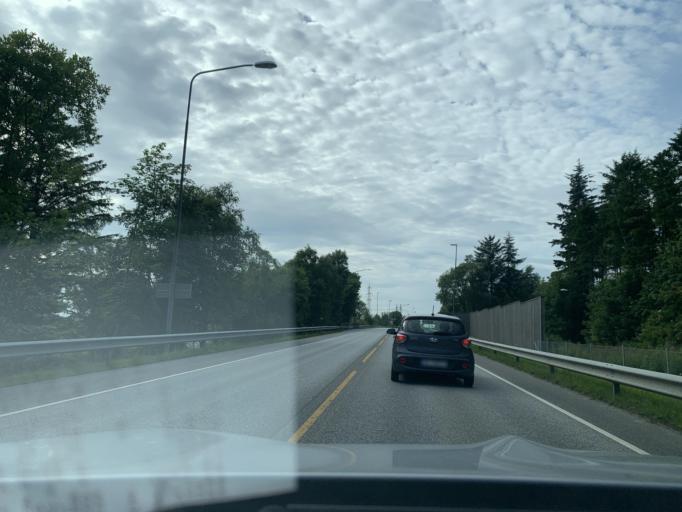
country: NO
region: Rogaland
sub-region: Stavanger
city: Stavanger
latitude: 58.9189
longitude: 5.7139
